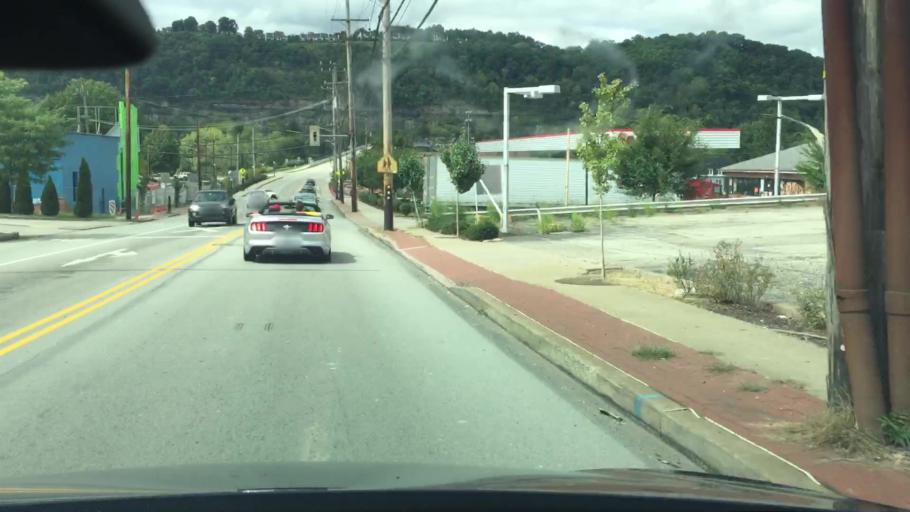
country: US
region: Pennsylvania
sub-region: Allegheny County
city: Oakmont
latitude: 40.5257
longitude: -79.8412
